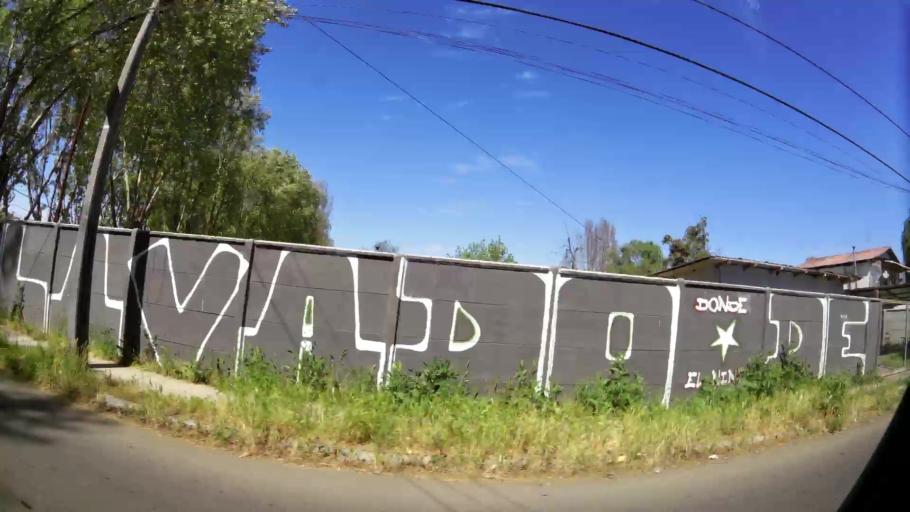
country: CL
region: Santiago Metropolitan
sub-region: Provincia de Talagante
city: Penaflor
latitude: -33.5979
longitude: -70.8788
